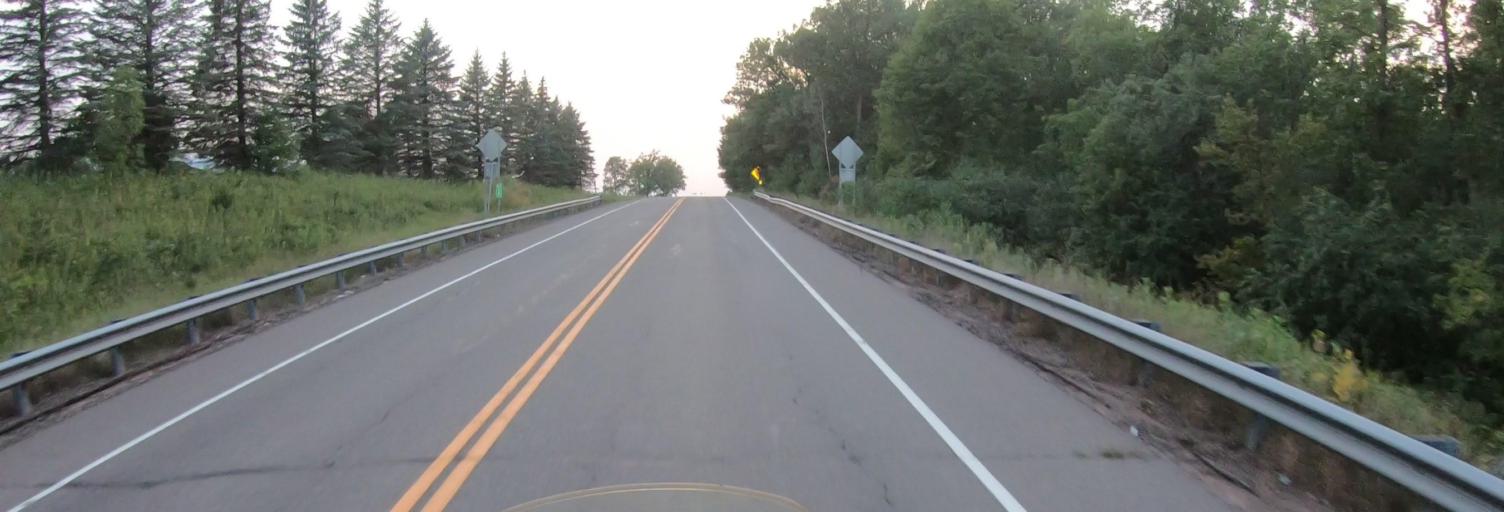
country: US
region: Minnesota
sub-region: Pine County
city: Rock Creek
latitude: 45.7664
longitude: -92.9638
